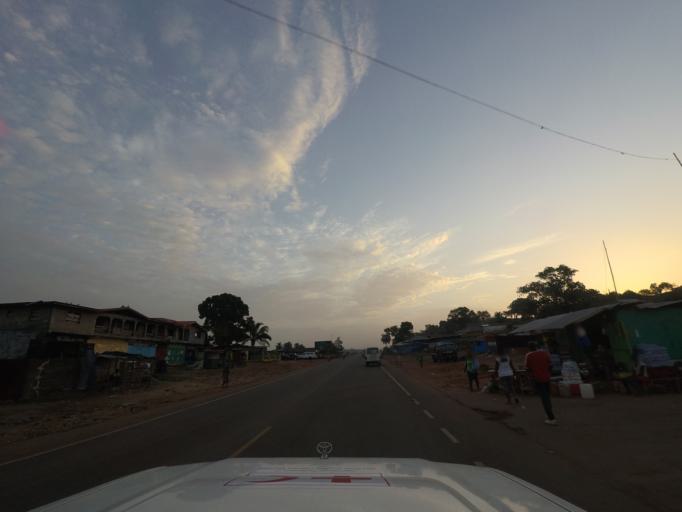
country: LR
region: Montserrado
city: Monrovia
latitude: 6.3100
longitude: -10.6701
